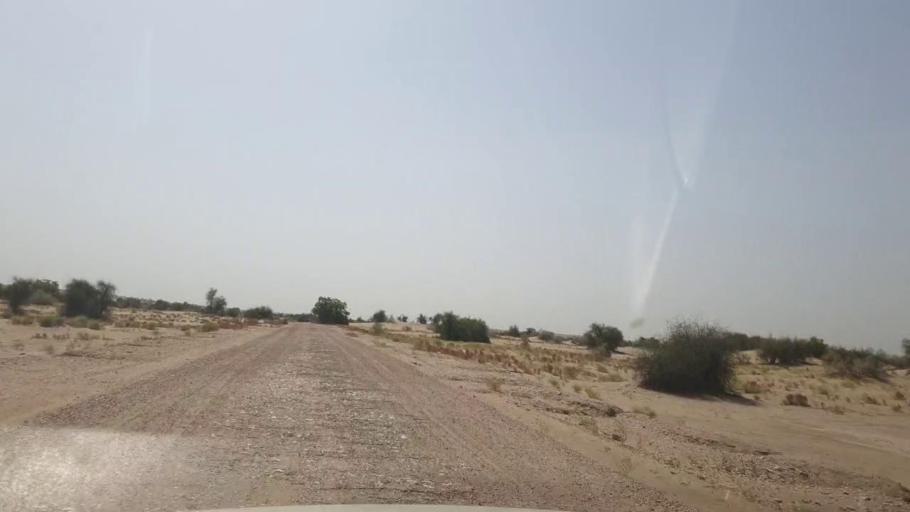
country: PK
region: Sindh
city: Khanpur
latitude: 27.4291
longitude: 69.2567
